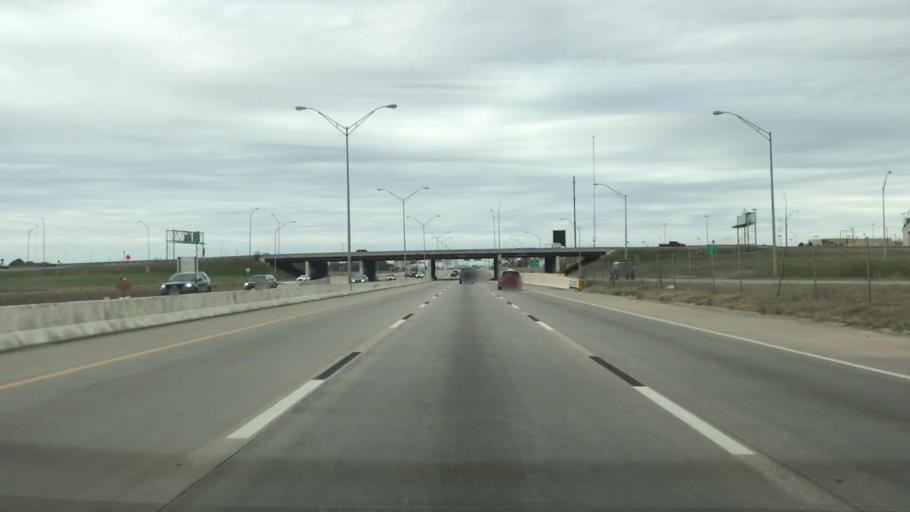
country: US
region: Oklahoma
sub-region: Cleveland County
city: Moore
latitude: 35.3899
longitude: -97.4950
